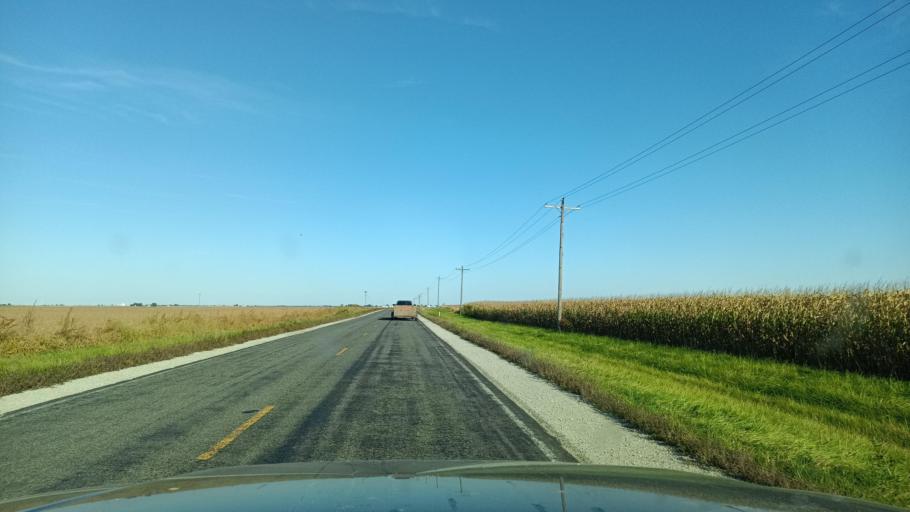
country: US
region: Illinois
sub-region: McLean County
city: Le Roy
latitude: 40.2245
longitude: -88.7894
